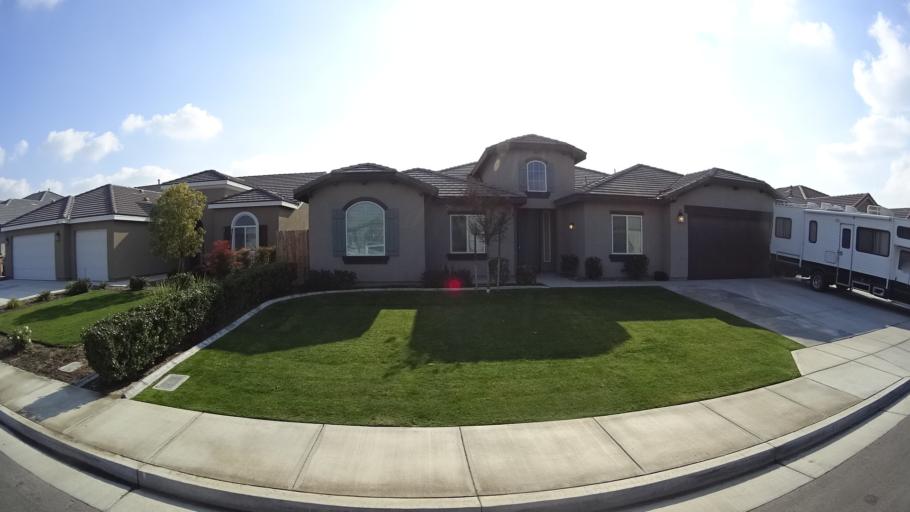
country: US
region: California
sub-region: Kern County
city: Greenacres
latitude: 35.2866
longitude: -119.1078
